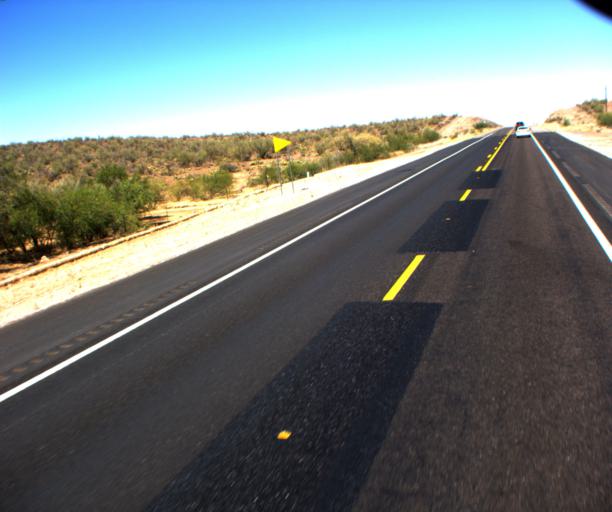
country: US
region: Arizona
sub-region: Pima County
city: Sells
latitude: 31.9167
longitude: -111.8505
